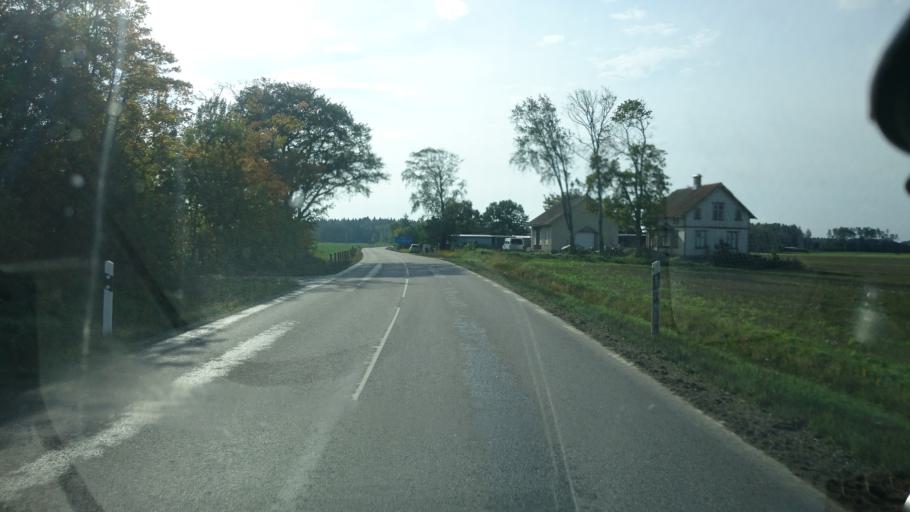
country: SE
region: Vaestra Goetaland
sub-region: Vanersborgs Kommun
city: Vargon
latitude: 58.2688
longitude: 12.4002
